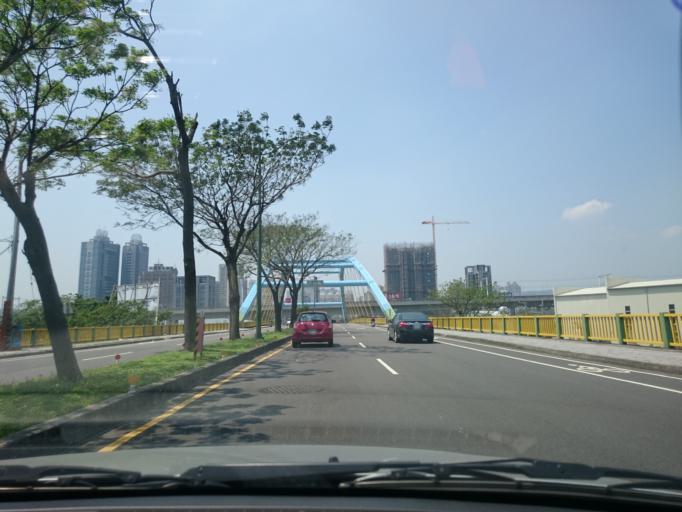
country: TW
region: Taiwan
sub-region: Taichung City
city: Taichung
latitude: 24.1805
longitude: 120.6304
